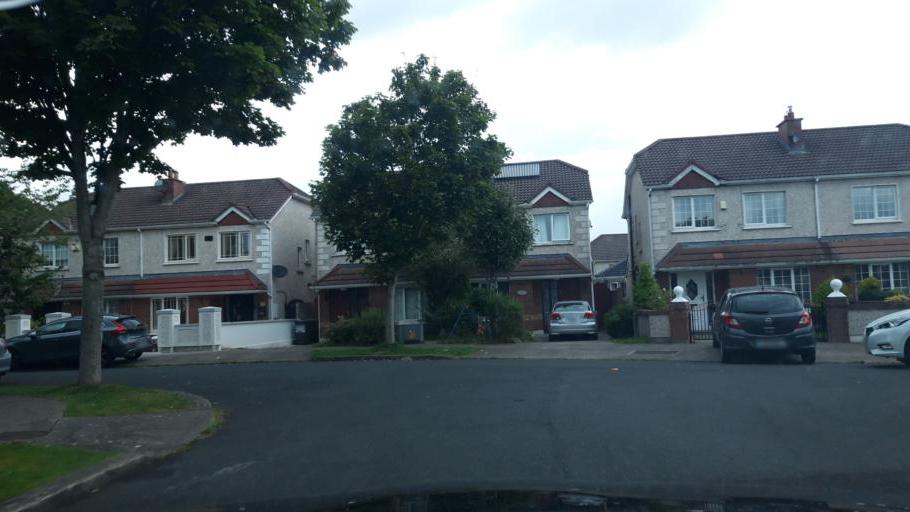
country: IE
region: Leinster
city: Hartstown
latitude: 53.4009
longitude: -6.4190
